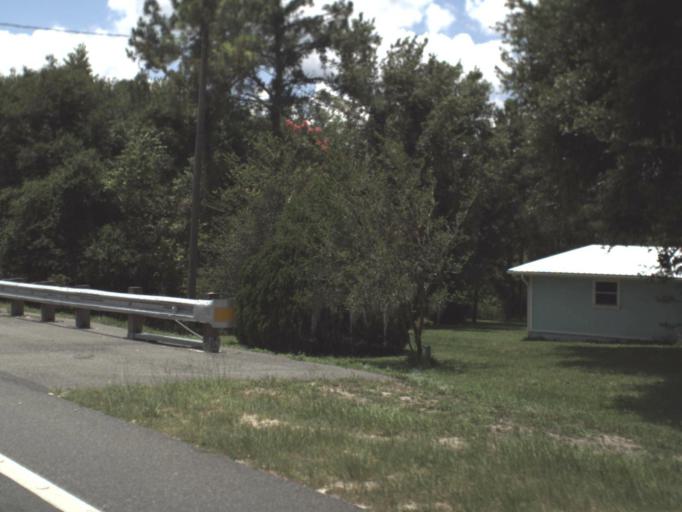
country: US
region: Florida
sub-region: Clay County
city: Keystone Heights
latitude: 29.7533
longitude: -81.9961
